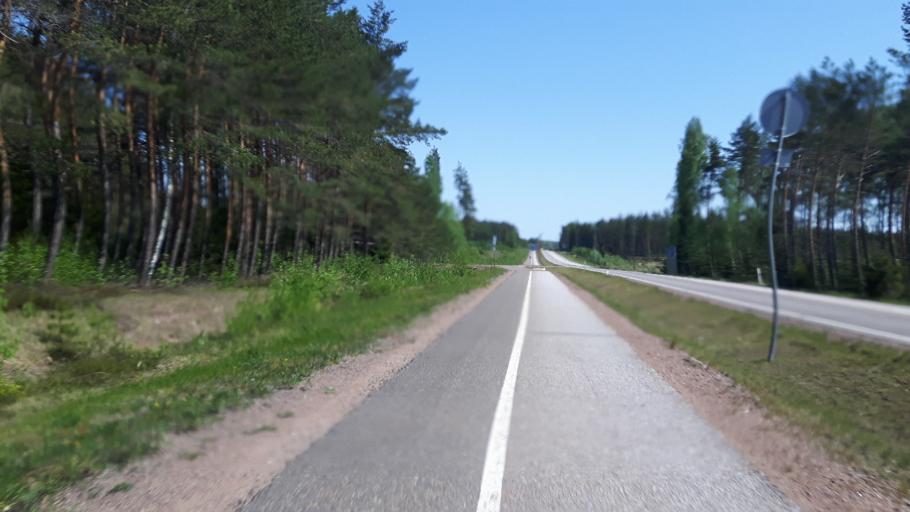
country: FI
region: Kymenlaakso
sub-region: Kotka-Hamina
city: Pyhtaeae
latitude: 60.4887
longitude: 26.5092
